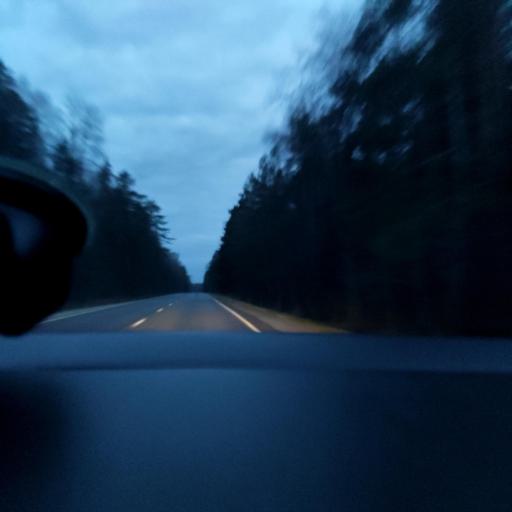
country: RU
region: Moskovskaya
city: Shaturtorf
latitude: 55.4300
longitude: 39.3768
